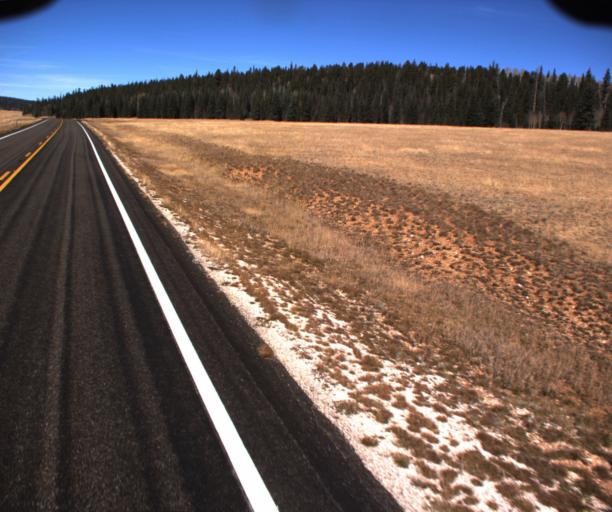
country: US
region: Arizona
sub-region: Coconino County
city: Grand Canyon
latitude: 36.3653
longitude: -112.1205
